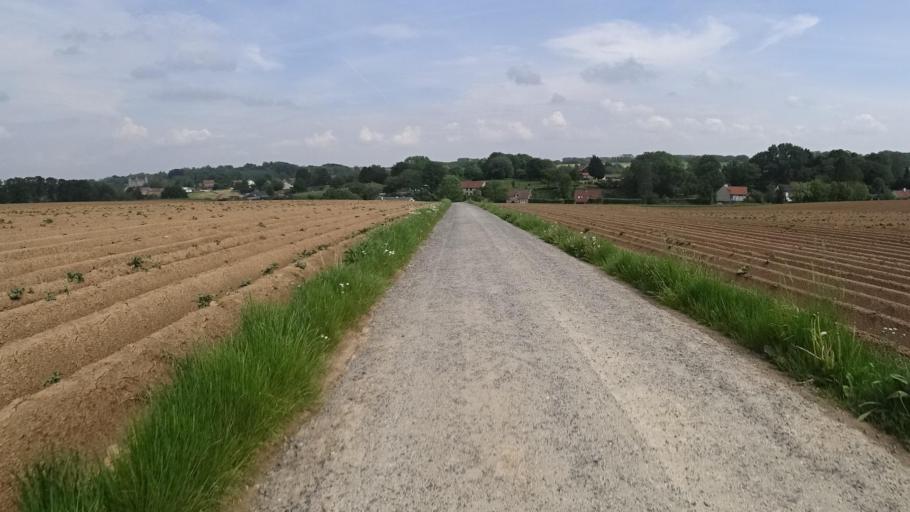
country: BE
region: Wallonia
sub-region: Province du Brabant Wallon
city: Louvain-la-Neuve
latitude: 50.6768
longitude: 4.6324
